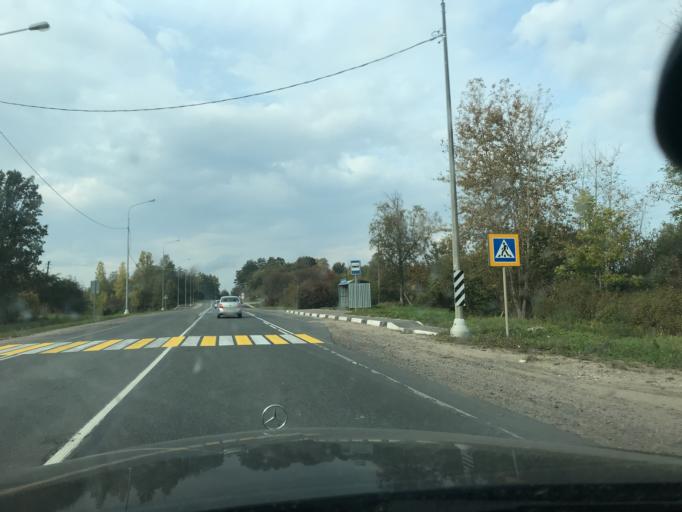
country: RU
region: Pskov
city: Ostrov
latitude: 57.3011
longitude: 28.3734
